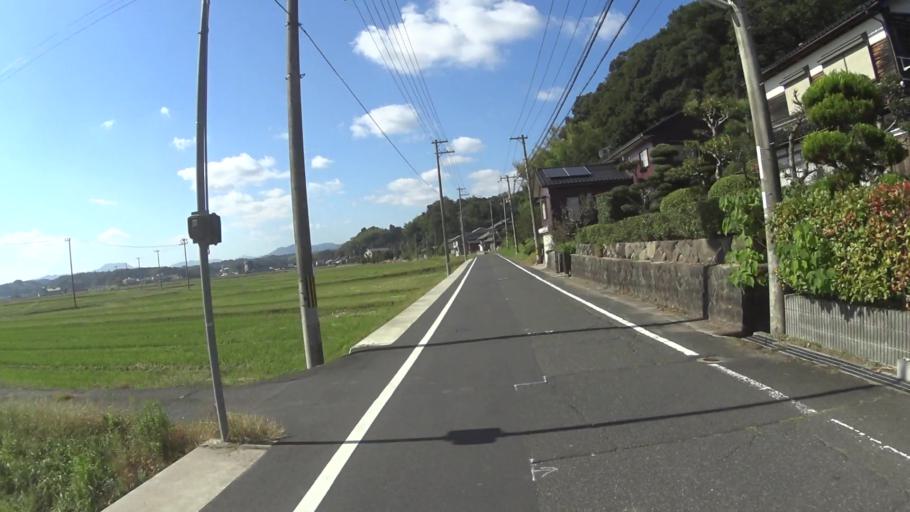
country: JP
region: Kyoto
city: Miyazu
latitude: 35.6796
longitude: 135.0874
